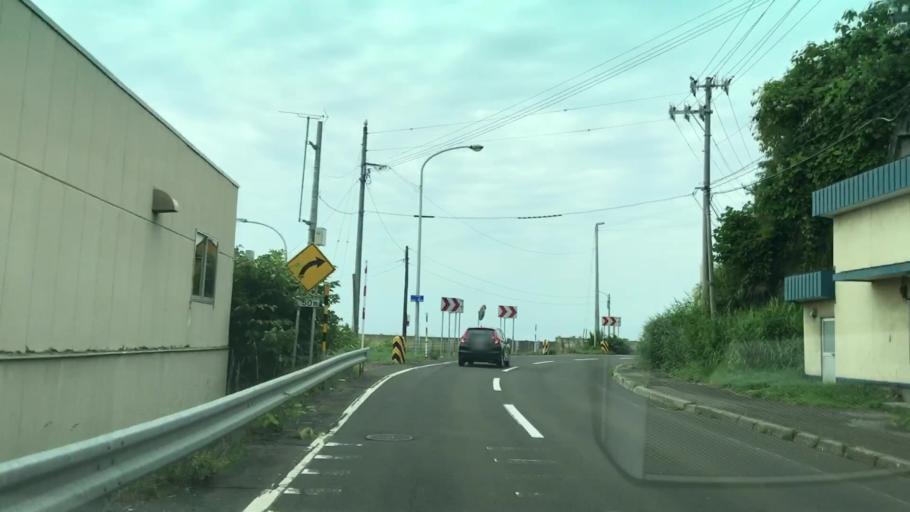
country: JP
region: Hokkaido
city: Iwanai
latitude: 43.1432
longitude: 140.4250
